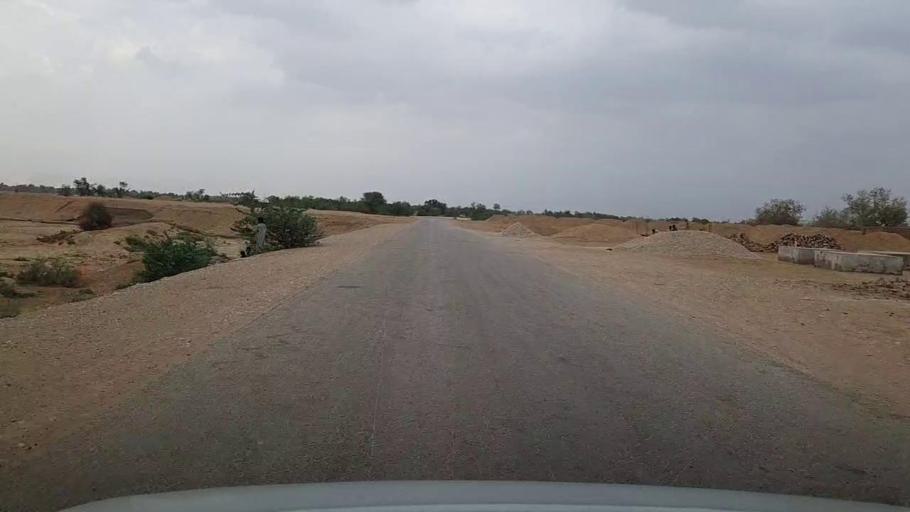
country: PK
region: Sindh
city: Sehwan
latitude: 26.3396
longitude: 67.7266
